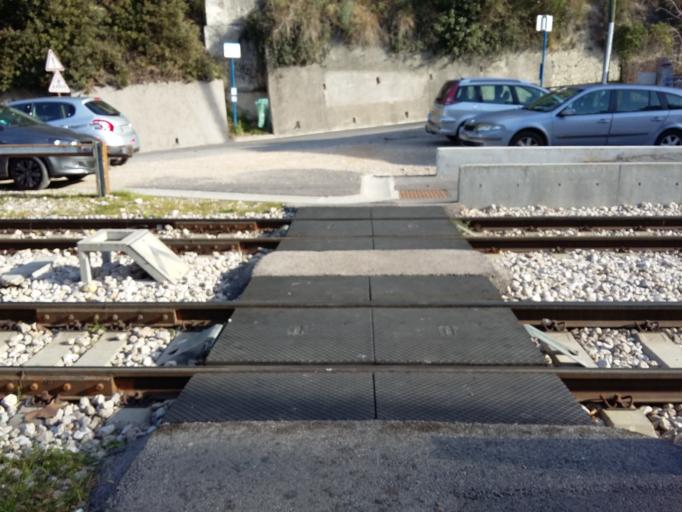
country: FR
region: Provence-Alpes-Cote d'Azur
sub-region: Departement des Alpes-Maritimes
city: Nice
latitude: 43.7086
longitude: 7.2316
